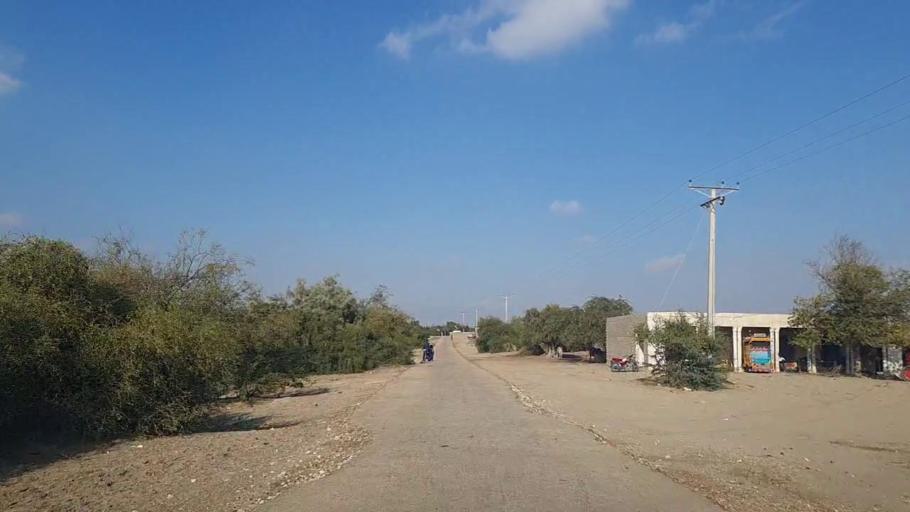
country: PK
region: Sindh
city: Tando Mittha Khan
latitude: 26.0139
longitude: 69.2485
